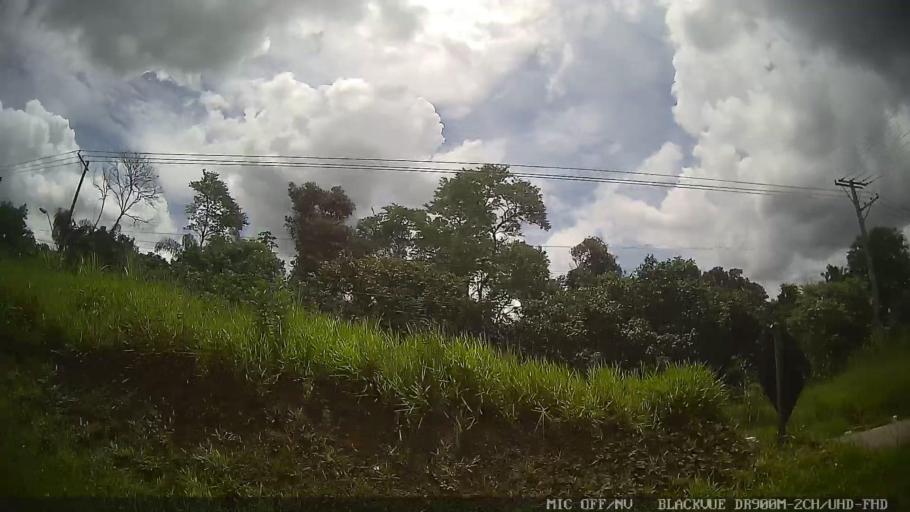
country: BR
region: Sao Paulo
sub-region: Suzano
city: Suzano
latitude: -23.6025
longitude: -46.3097
